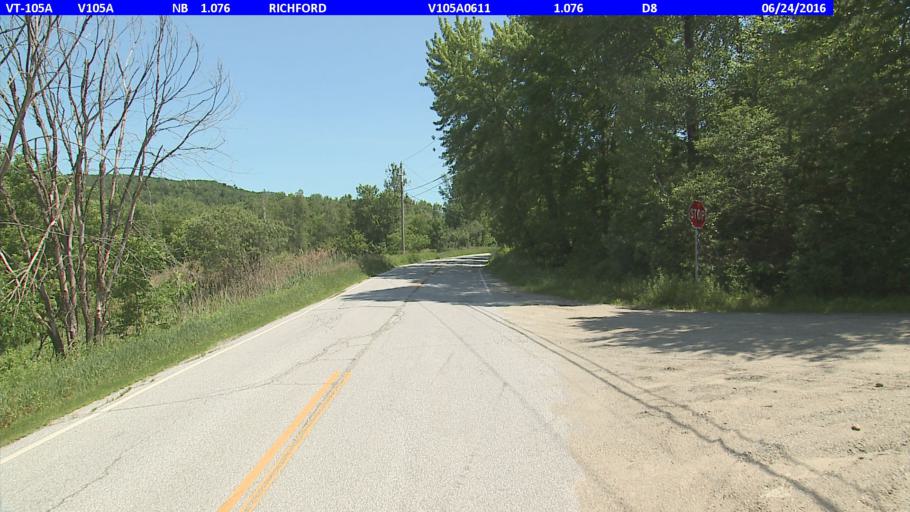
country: US
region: Vermont
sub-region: Franklin County
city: Richford
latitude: 45.0045
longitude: -72.5971
